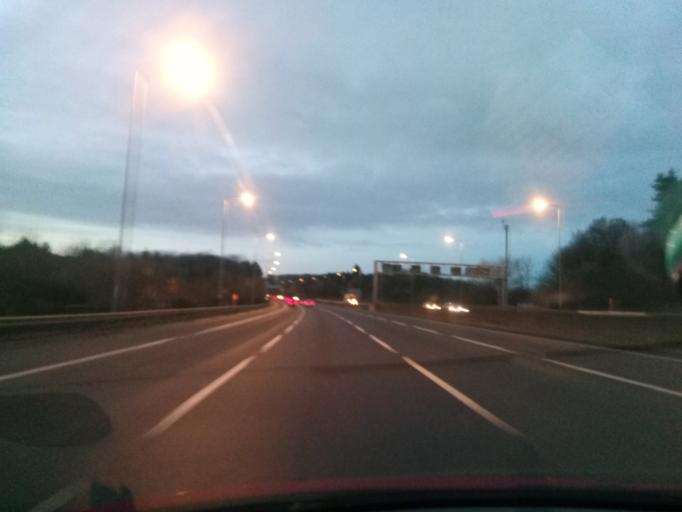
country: GB
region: England
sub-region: Nottinghamshire
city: Kirkby in Ashfield
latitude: 53.0531
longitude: -1.2580
